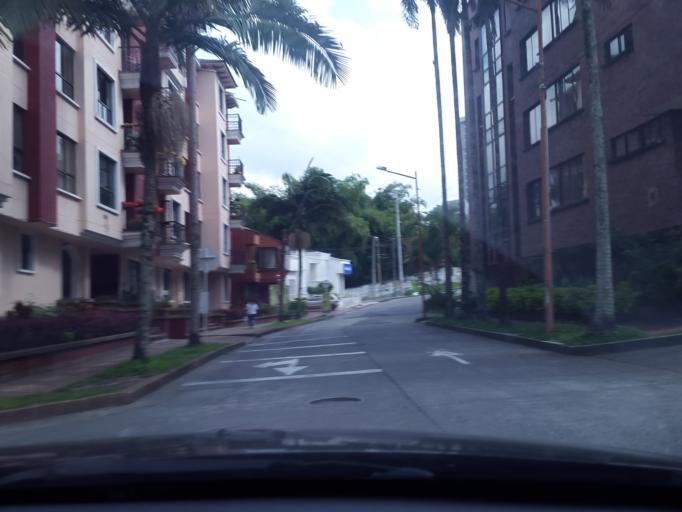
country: CO
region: Quindio
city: Armenia
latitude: 4.5485
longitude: -75.6623
